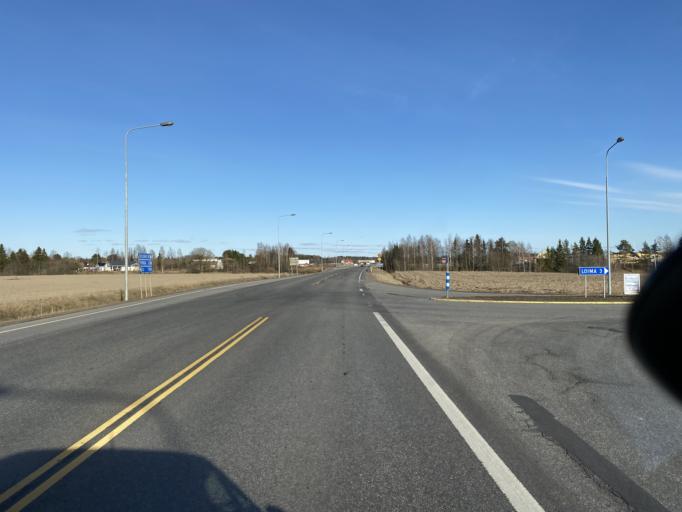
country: FI
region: Satakunta
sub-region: Pori
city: Huittinen
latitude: 61.1685
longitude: 22.6842
